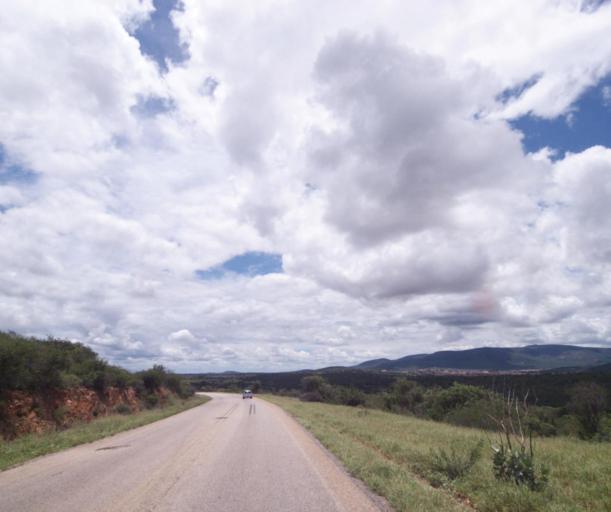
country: BR
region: Bahia
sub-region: Brumado
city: Brumado
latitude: -14.1997
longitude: -41.6159
